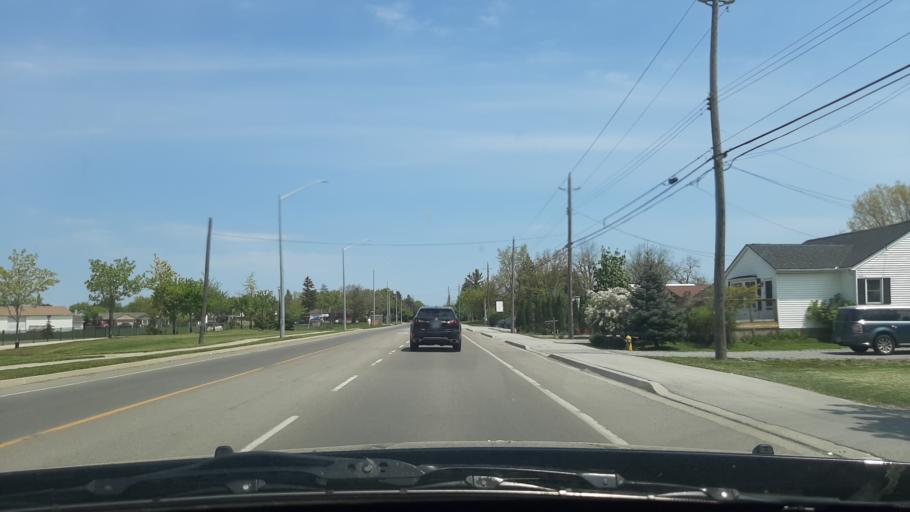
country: US
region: New York
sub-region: Niagara County
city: Youngstown
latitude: 43.2158
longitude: -79.1301
